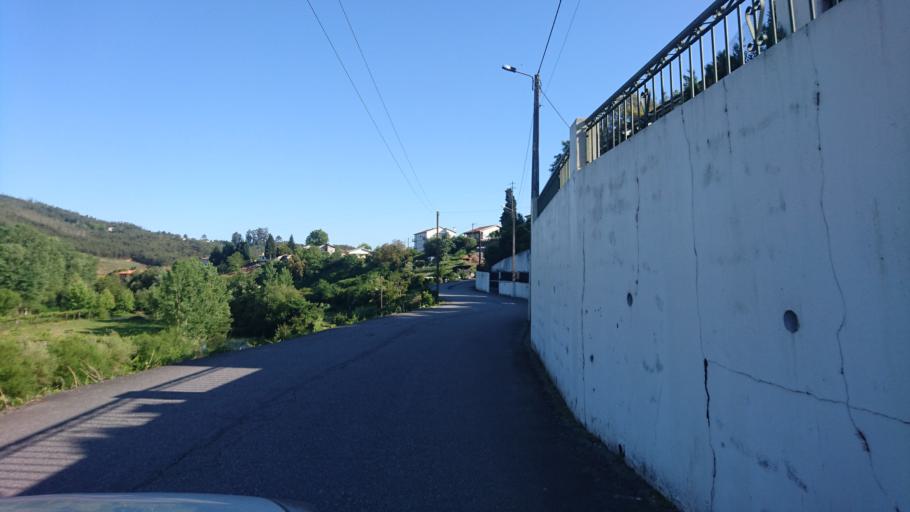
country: PT
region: Porto
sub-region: Paredes
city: Recarei
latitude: 41.1491
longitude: -8.3886
